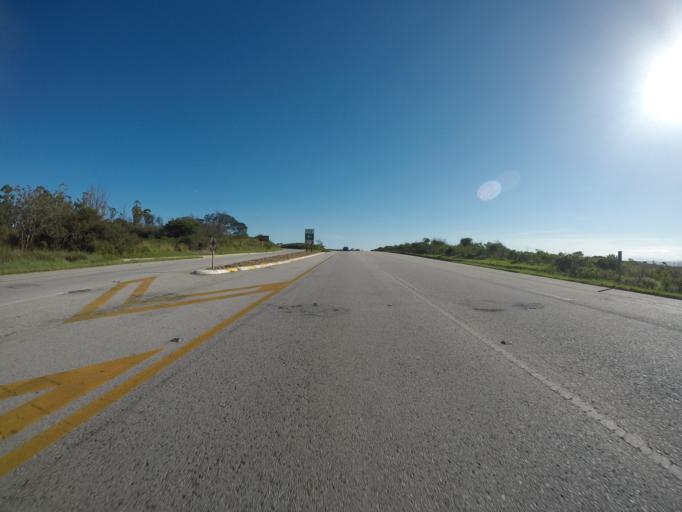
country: ZA
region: Eastern Cape
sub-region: Cacadu District Municipality
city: Jeffrey's Bay
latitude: -33.8956
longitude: 25.1252
